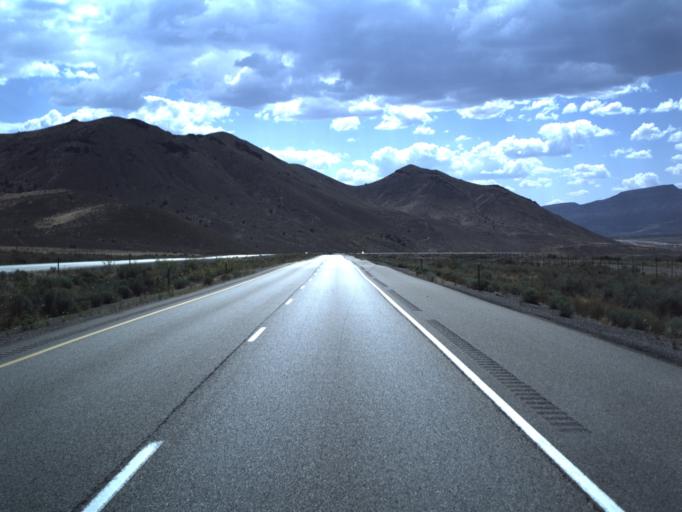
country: US
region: Utah
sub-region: Sevier County
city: Aurora
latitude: 38.8846
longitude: -111.9195
